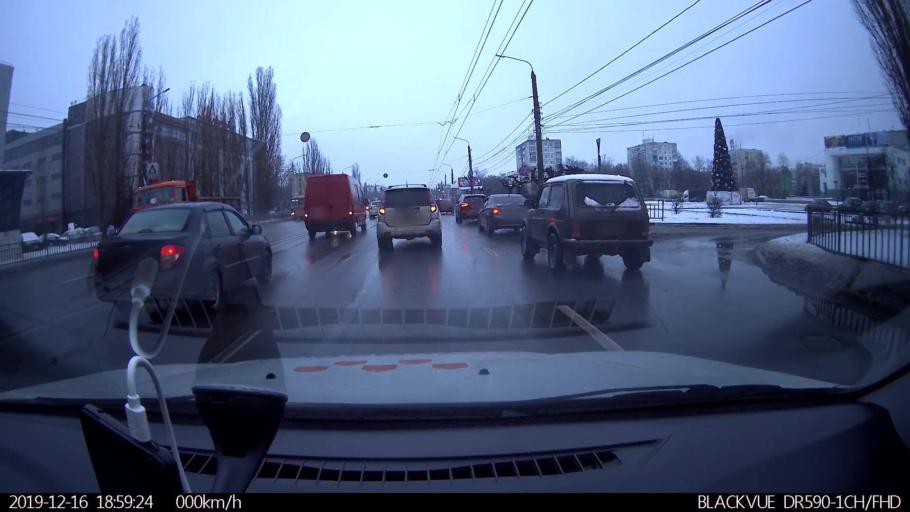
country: RU
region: Nizjnij Novgorod
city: Nizhniy Novgorod
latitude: 56.2860
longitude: 43.9287
